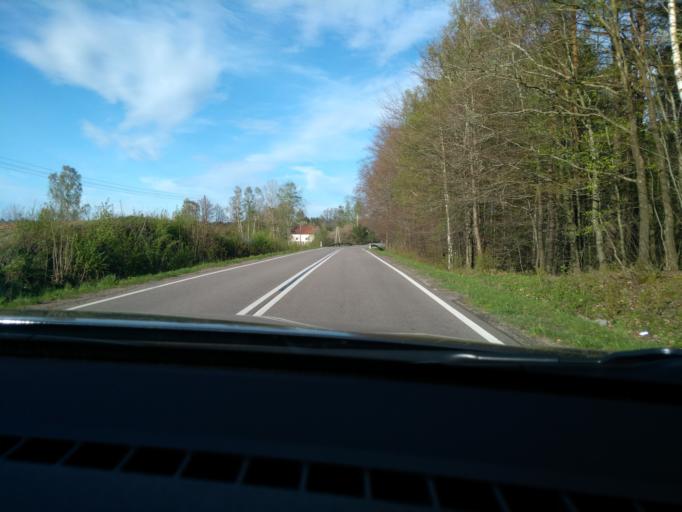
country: PL
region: Pomeranian Voivodeship
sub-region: Powiat leborski
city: Cewice
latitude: 54.3383
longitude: 17.7377
